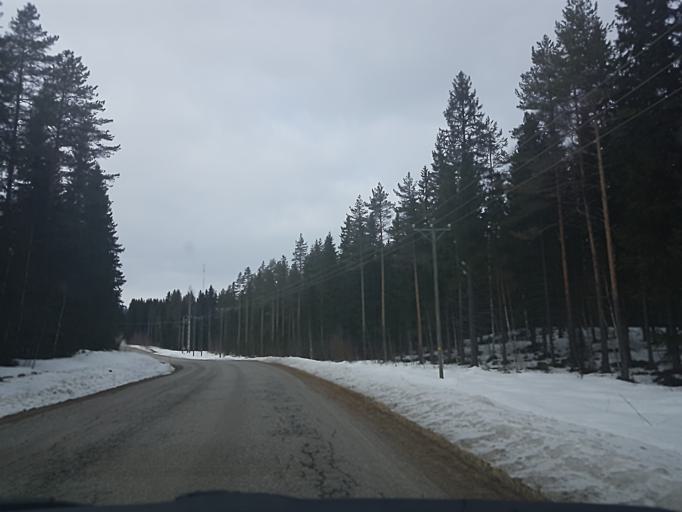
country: FI
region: Northern Savo
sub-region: Koillis-Savo
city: Kaavi
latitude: 63.0200
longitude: 28.6494
